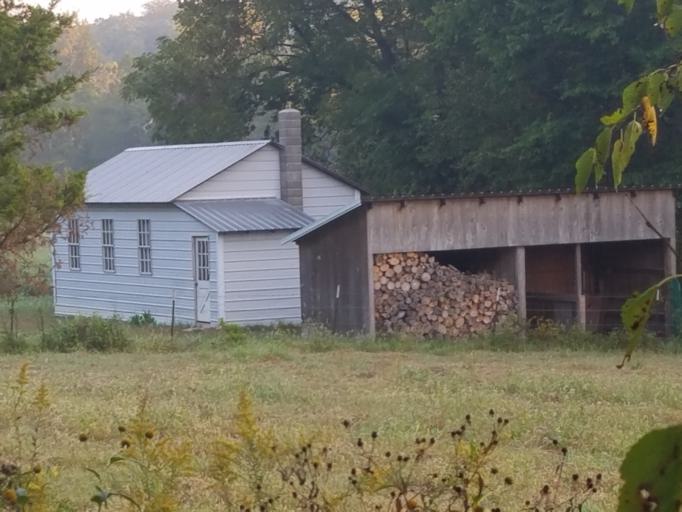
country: US
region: Missouri
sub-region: Moniteau County
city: California
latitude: 38.7461
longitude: -92.6289
